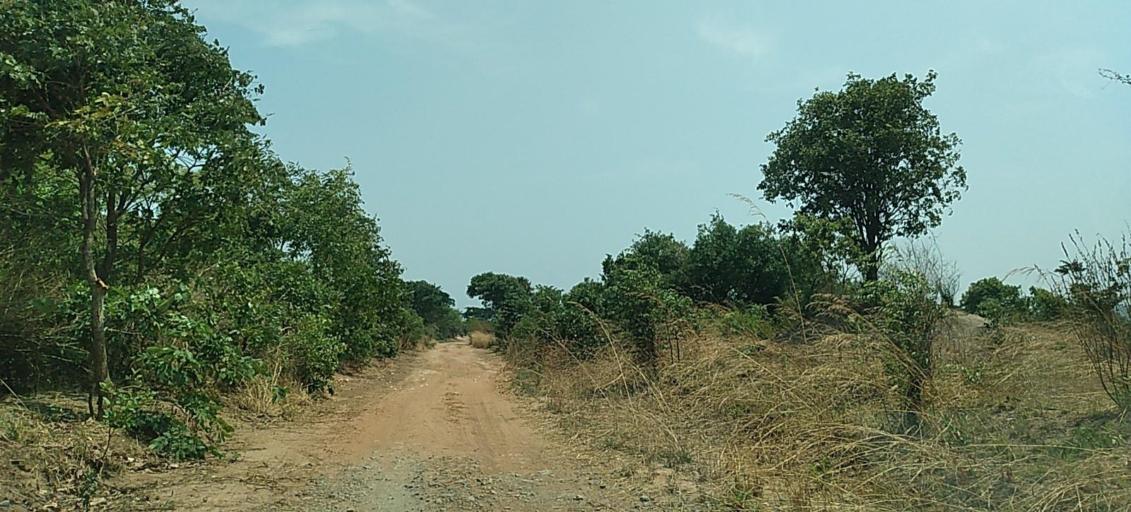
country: ZM
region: Copperbelt
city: Ndola
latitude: -13.0907
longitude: 28.7453
